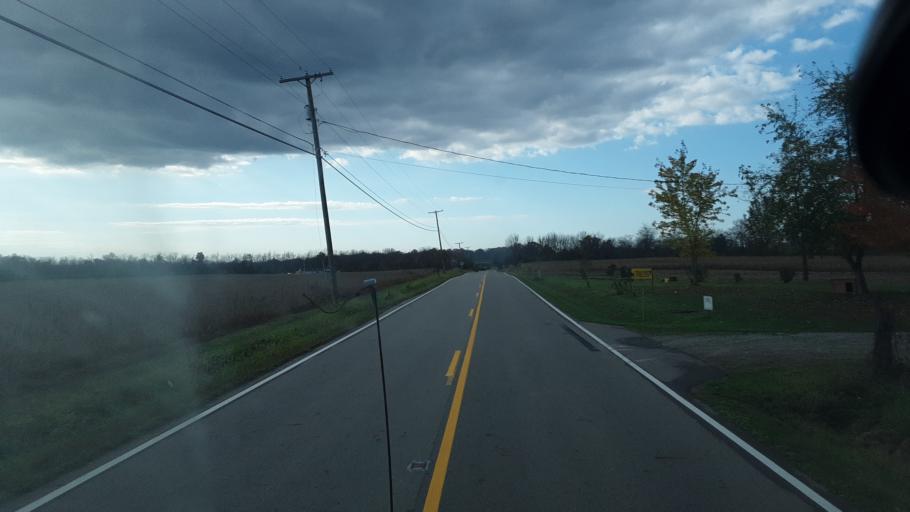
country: US
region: Ohio
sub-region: Highland County
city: Greenfield
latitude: 39.3875
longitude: -83.4676
